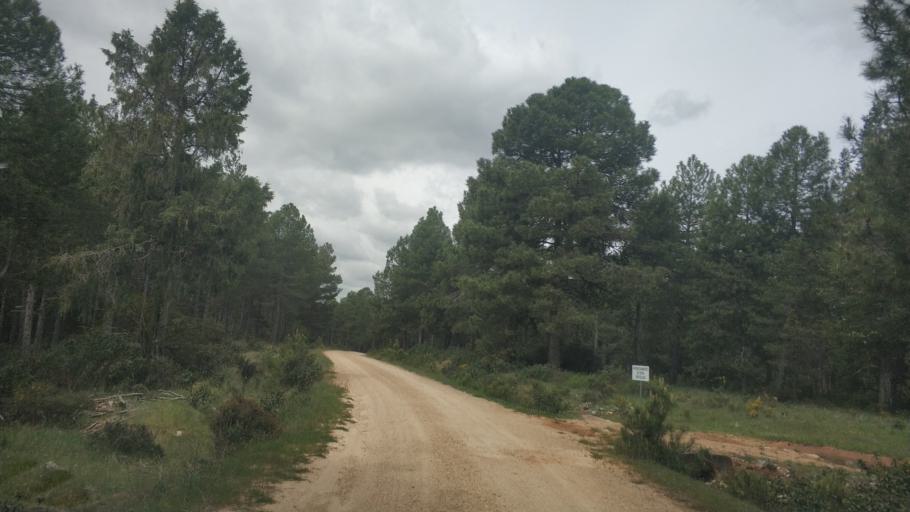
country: ES
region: Castille and Leon
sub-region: Provincia de Soria
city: Casarejos
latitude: 41.7735
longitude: -3.0416
